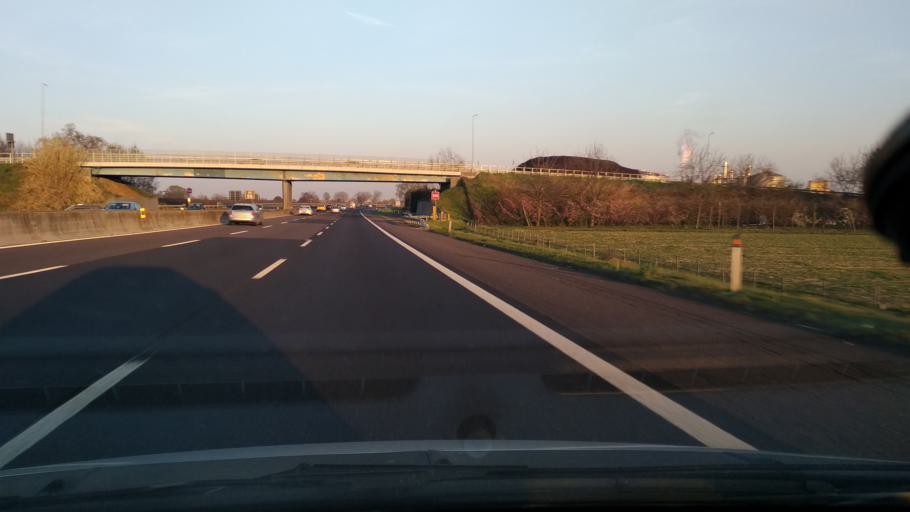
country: IT
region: Emilia-Romagna
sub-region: Provincia di Ravenna
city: Solarolo
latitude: 44.3384
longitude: 11.8651
